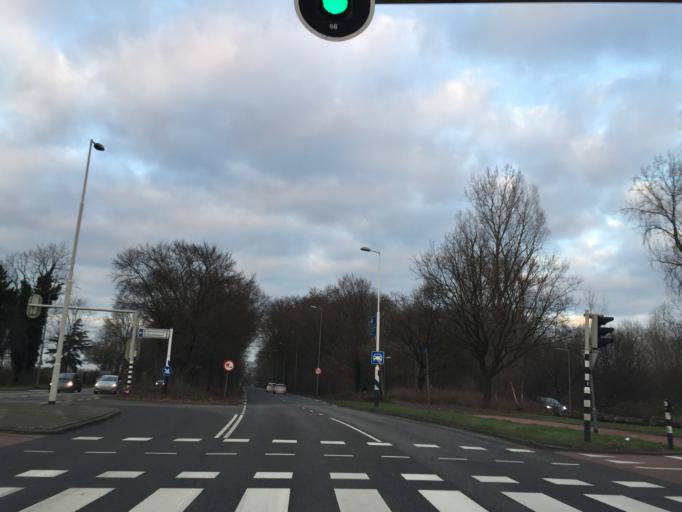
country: NL
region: South Holland
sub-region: Gemeente Rotterdam
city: Rotterdam
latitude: 51.9380
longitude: 4.5015
